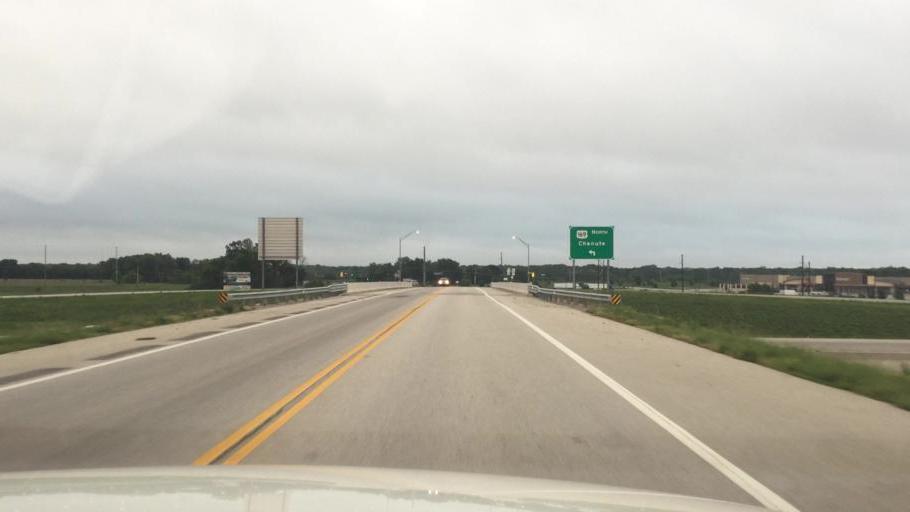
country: US
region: Kansas
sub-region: Montgomery County
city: Coffeyville
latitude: 37.0468
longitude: -95.5832
